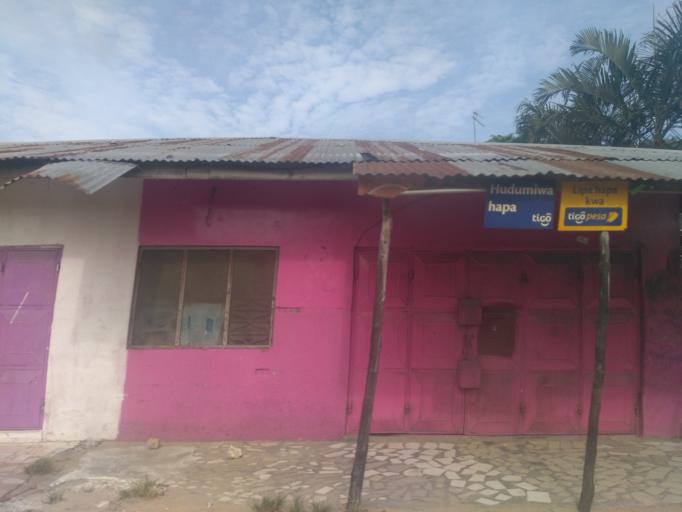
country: TZ
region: Zanzibar Urban/West
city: Zanzibar
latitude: -6.1686
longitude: 39.2095
